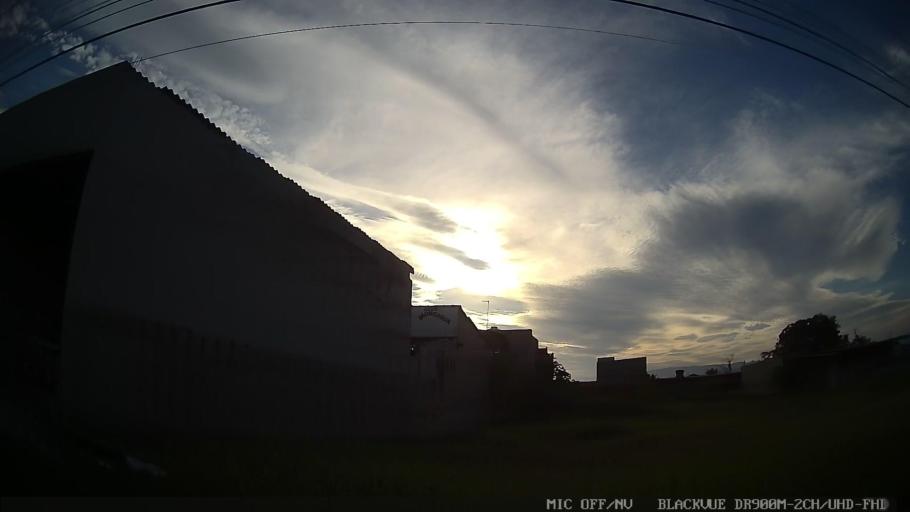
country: BR
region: Sao Paulo
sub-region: Itanhaem
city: Itanhaem
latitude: -24.1567
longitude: -46.7809
